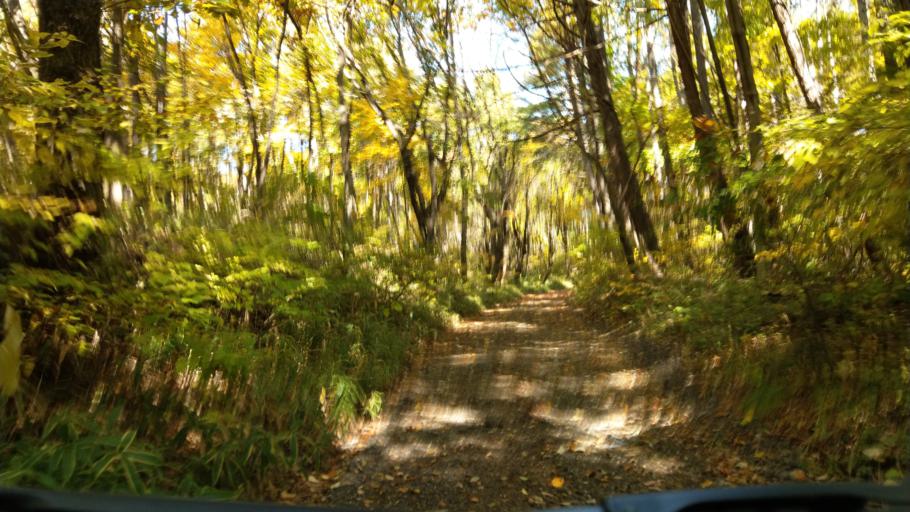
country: JP
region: Nagano
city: Komoro
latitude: 36.3653
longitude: 138.4526
